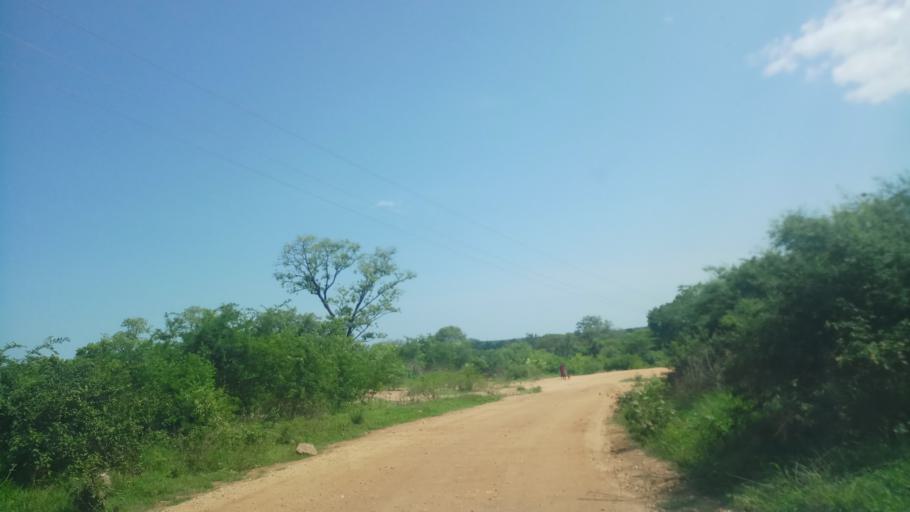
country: ET
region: Gambela
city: Gambela
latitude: 8.2133
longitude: 34.5607
